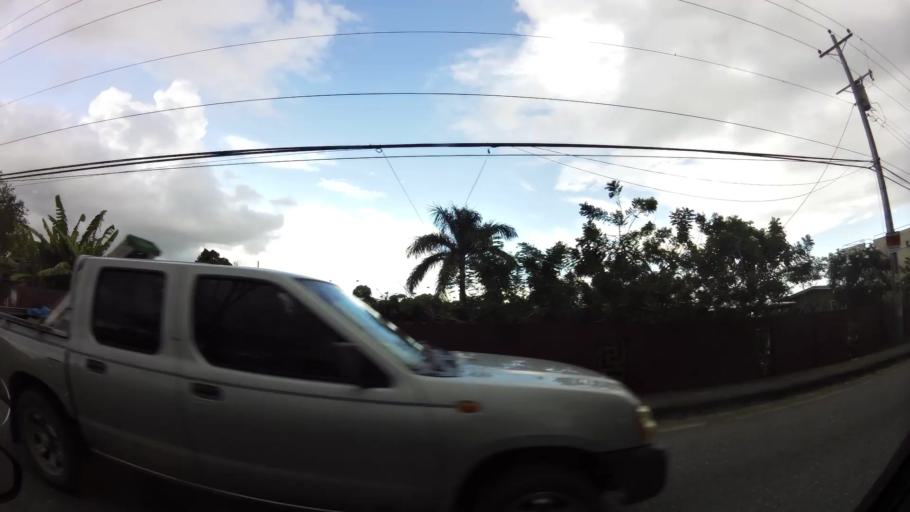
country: TT
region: City of San Fernando
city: Mon Repos
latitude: 10.2480
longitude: -61.4569
